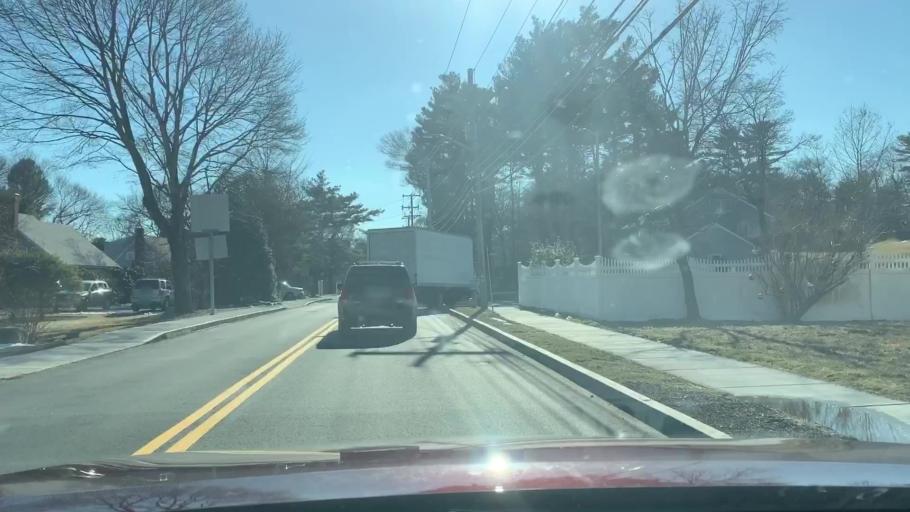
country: US
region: Massachusetts
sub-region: Essex County
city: Beverly Cove
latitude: 42.5691
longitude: -70.8593
